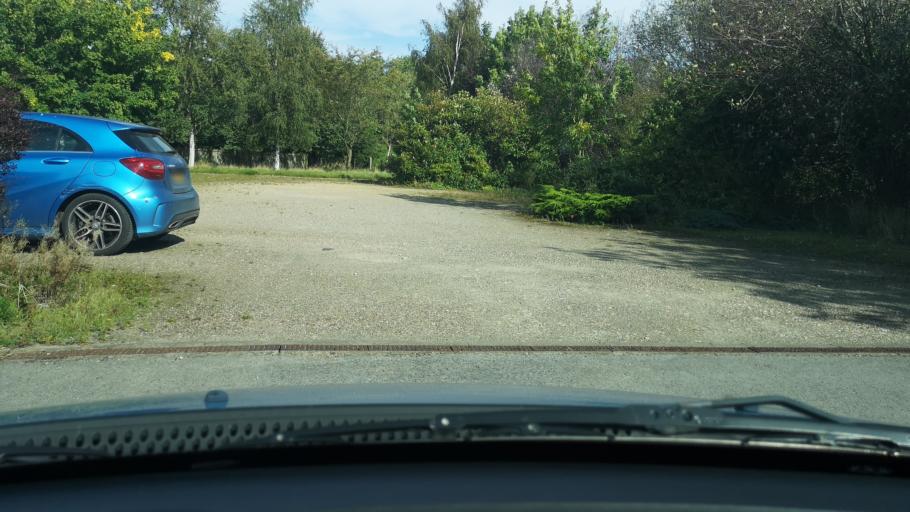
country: GB
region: England
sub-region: City and Borough of Wakefield
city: Walton
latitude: 53.6423
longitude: -1.4499
